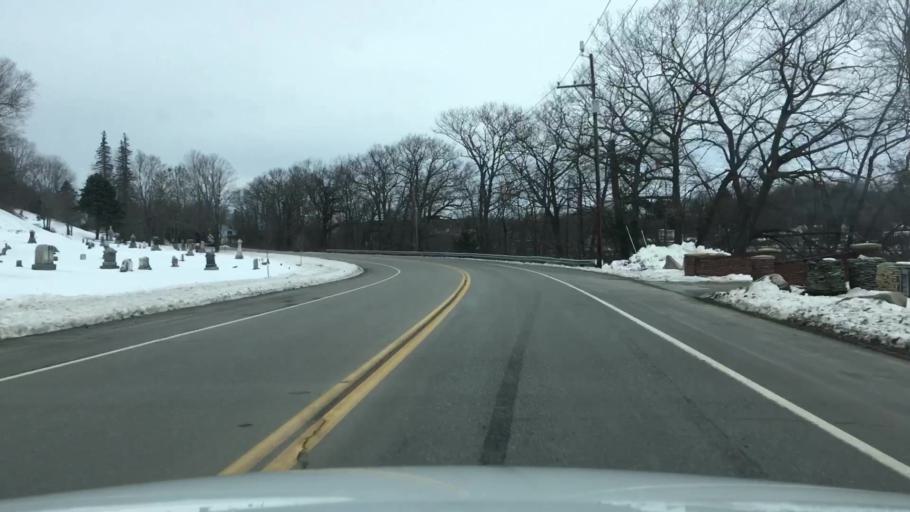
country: US
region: Maine
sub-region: Androscoggin County
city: Lewiston
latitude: 44.0798
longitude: -70.2109
